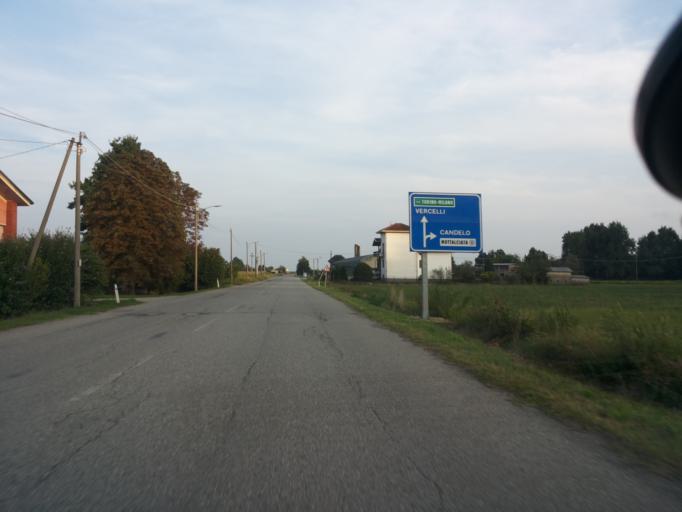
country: IT
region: Piedmont
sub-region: Provincia di Biella
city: Mottalciata
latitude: 45.5128
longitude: 8.2059
